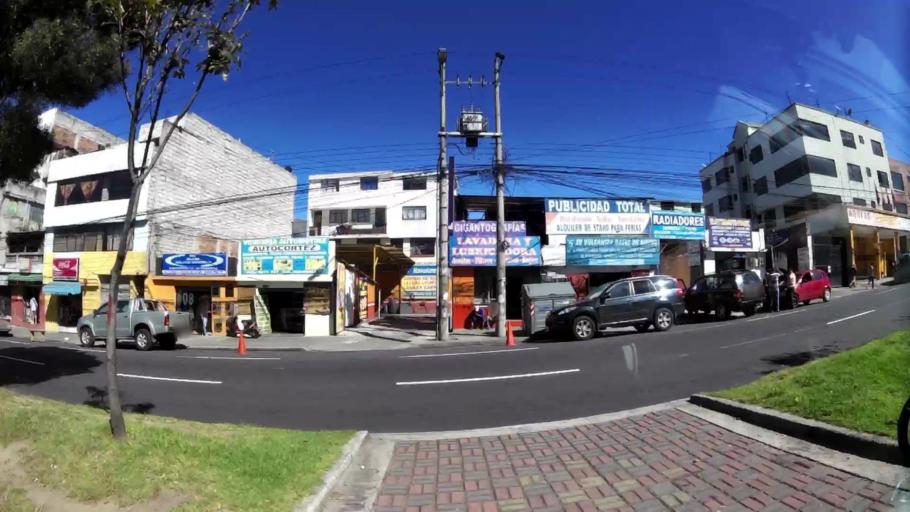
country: EC
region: Pichincha
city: Quito
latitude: -0.1476
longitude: -78.4751
